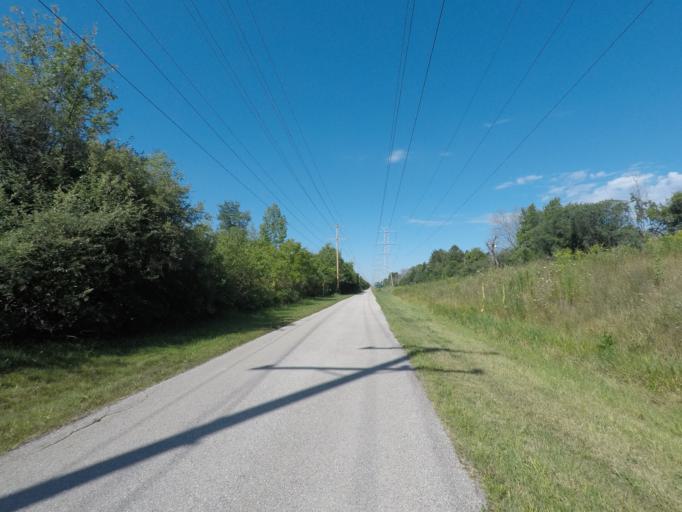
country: US
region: Wisconsin
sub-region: Waukesha County
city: New Berlin
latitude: 43.0101
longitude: -88.1331
